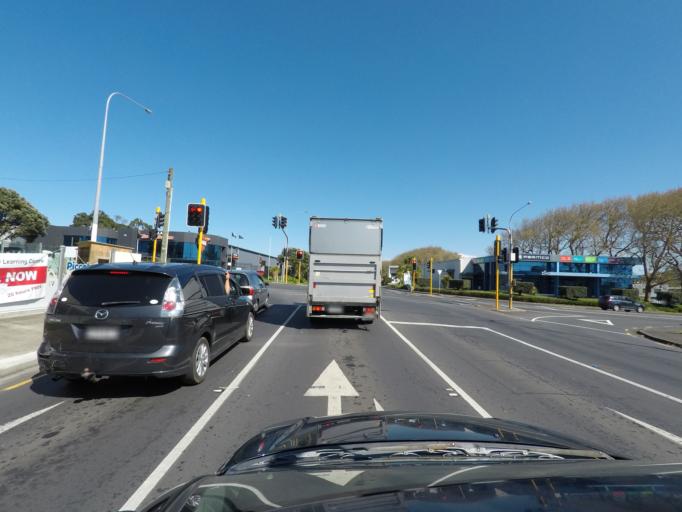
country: NZ
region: Auckland
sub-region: Auckland
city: Tamaki
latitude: -36.9277
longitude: 174.8427
